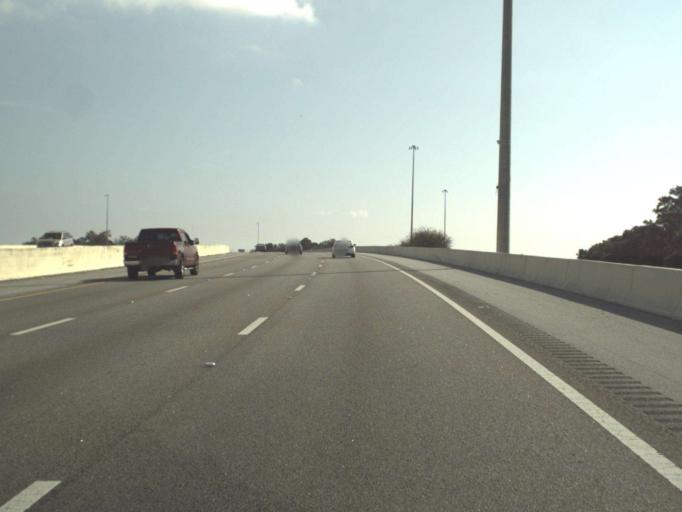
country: US
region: Florida
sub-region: Escambia County
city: Goulding
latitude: 30.4542
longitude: -87.2234
